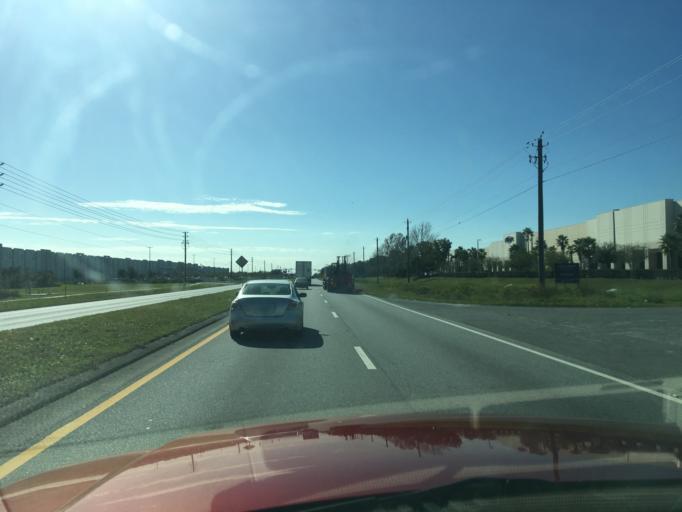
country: US
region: Florida
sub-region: Polk County
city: Winston
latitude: 28.0241
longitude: -82.0558
